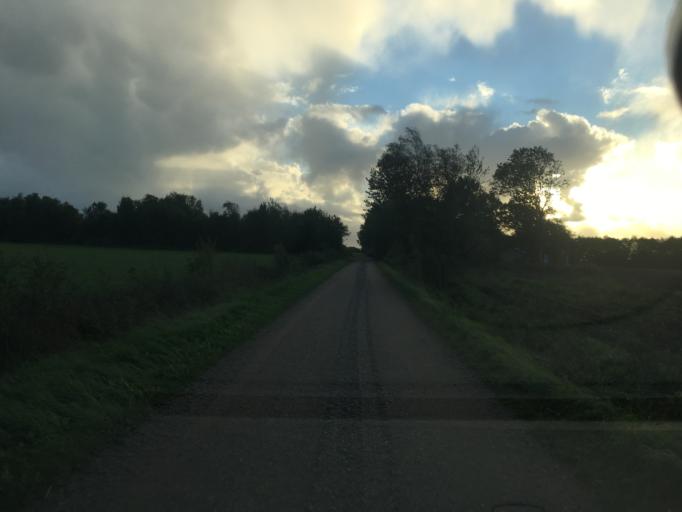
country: DE
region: Schleswig-Holstein
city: Ellhoft
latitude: 54.9445
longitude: 9.0114
